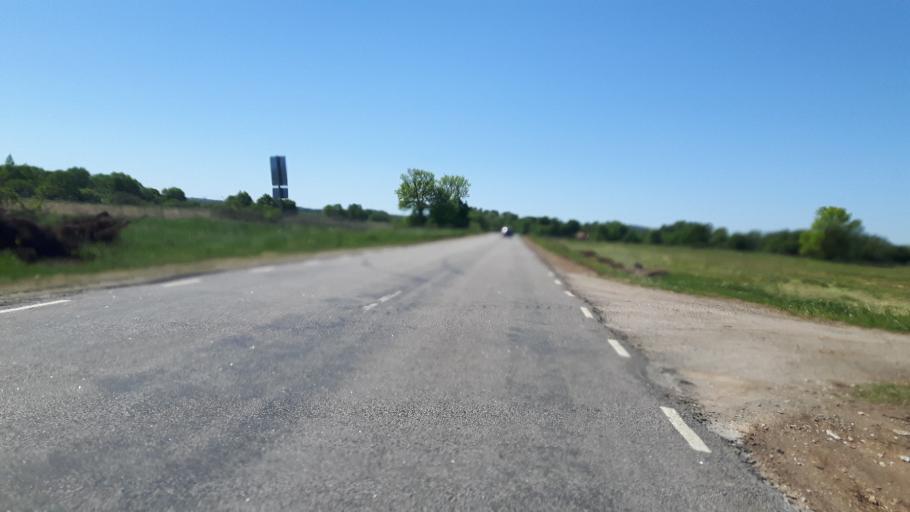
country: EE
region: Ida-Virumaa
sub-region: Narva-Joesuu linn
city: Narva-Joesuu
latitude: 59.3968
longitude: 27.9291
